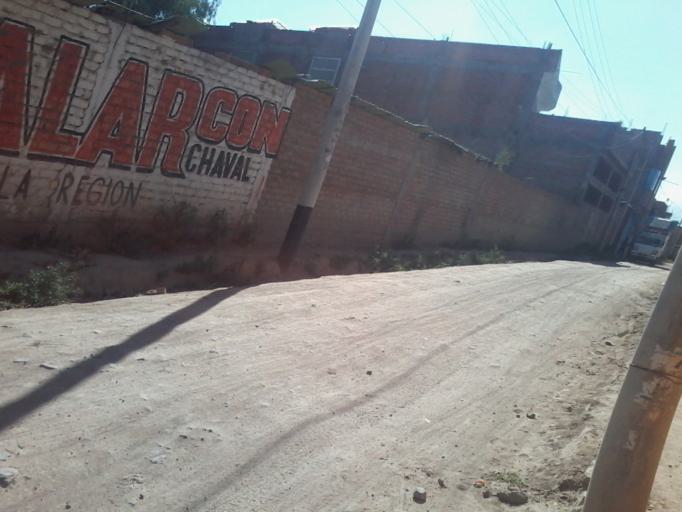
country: PE
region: Ayacucho
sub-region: Provincia de Huamanga
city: Ayacucho
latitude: -13.1635
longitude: -74.2107
